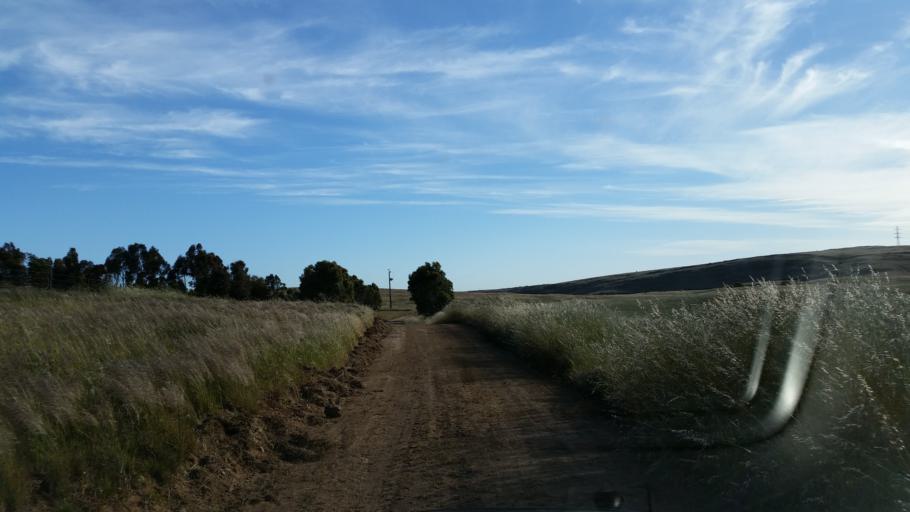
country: AU
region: South Australia
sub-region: Barossa
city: Angaston
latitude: -34.6844
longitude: 139.1730
